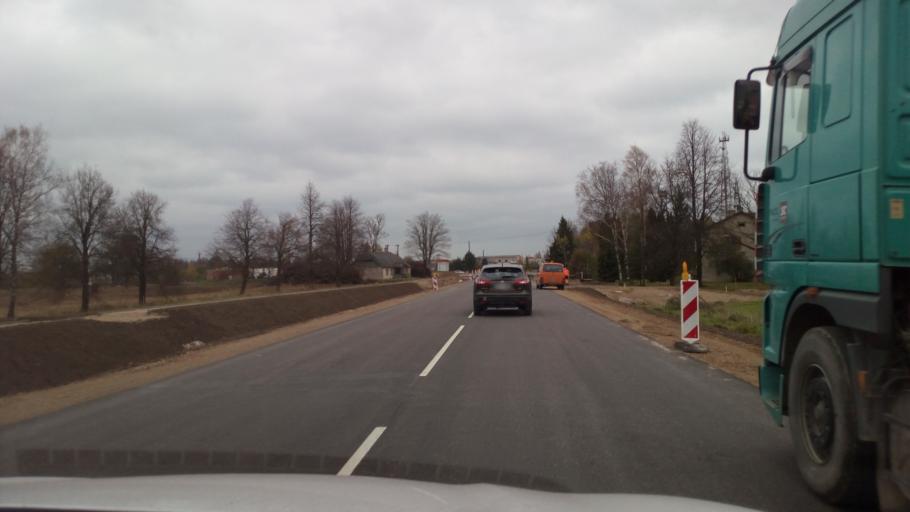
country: LV
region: Talsu Rajons
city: Talsi
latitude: 57.2300
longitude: 22.5853
